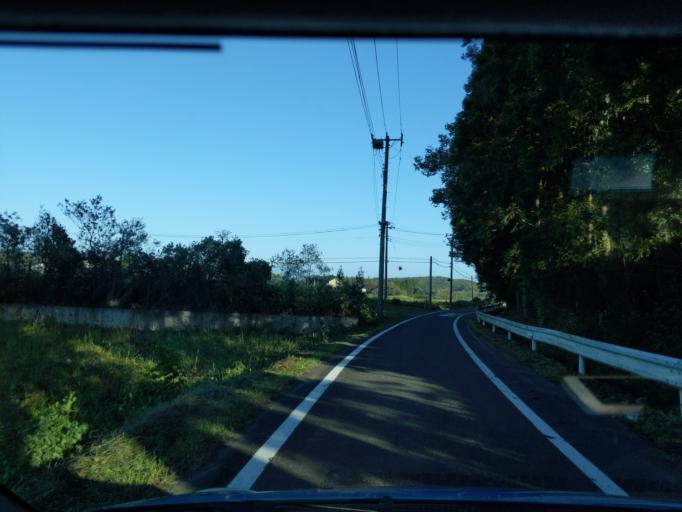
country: JP
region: Iwate
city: Ichinoseki
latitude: 38.9418
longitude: 141.0471
